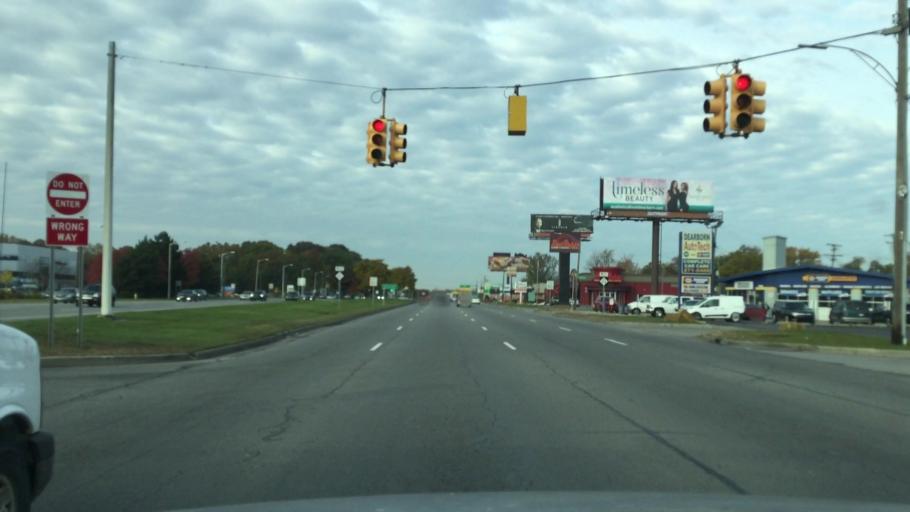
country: US
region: Michigan
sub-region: Wayne County
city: Dearborn
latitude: 42.3290
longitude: -83.2201
